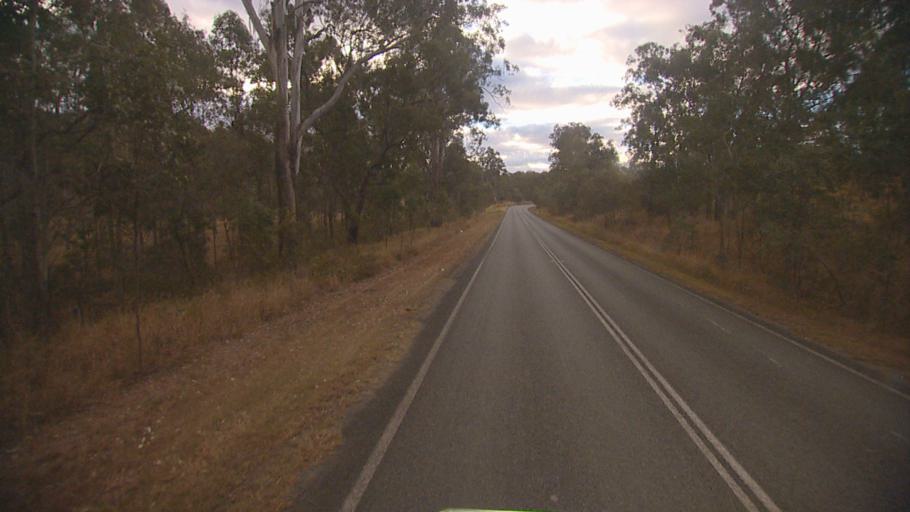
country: AU
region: Queensland
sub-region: Logan
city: Cedar Vale
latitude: -27.8986
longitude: 153.0891
